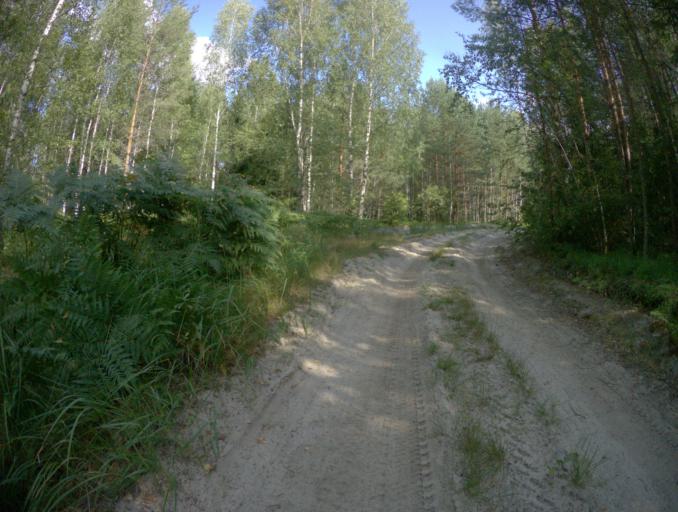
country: RU
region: Vladimir
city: Vorsha
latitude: 55.9111
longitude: 40.1593
